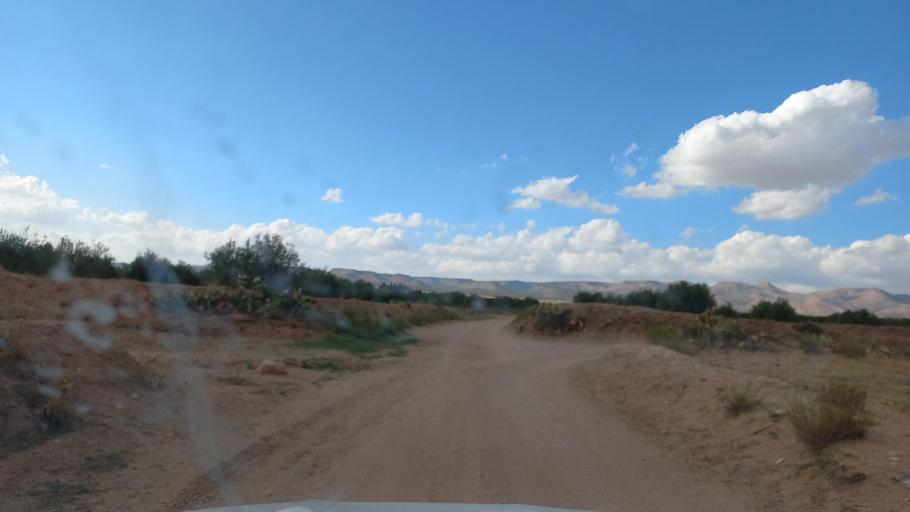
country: TN
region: Al Qasrayn
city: Sbiba
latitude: 35.3891
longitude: 9.0398
